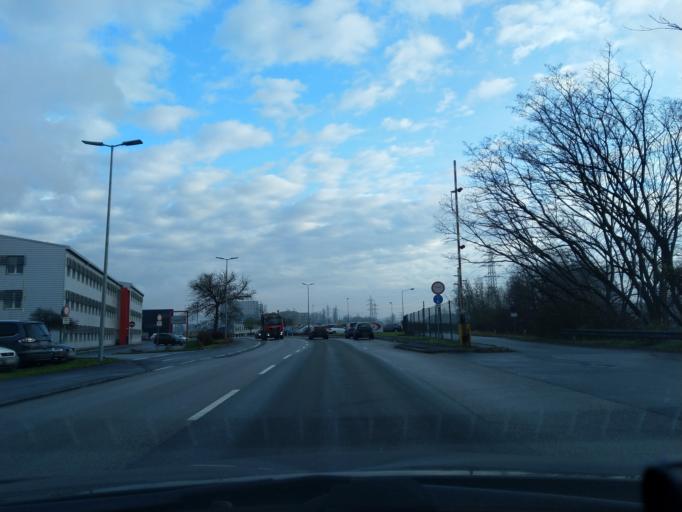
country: AT
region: Upper Austria
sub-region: Politischer Bezirk Urfahr-Umgebung
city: Steyregg
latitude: 48.2610
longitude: 14.3354
